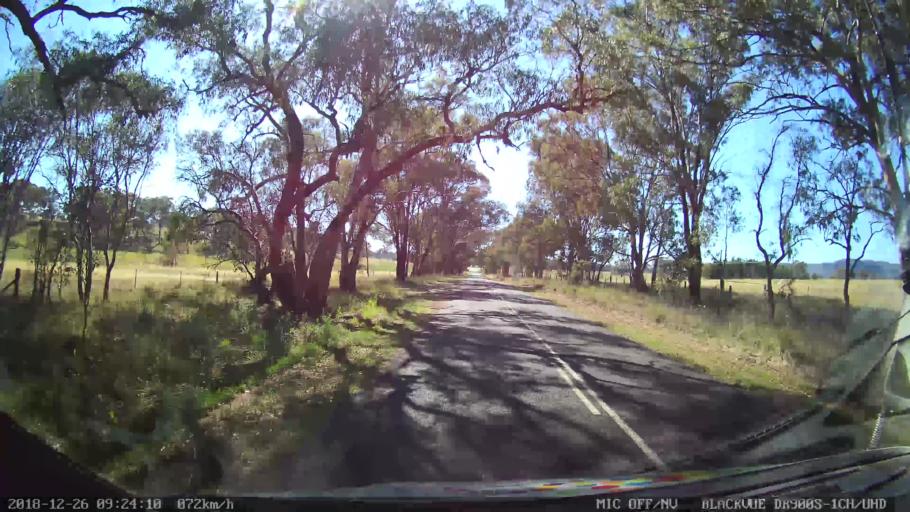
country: AU
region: New South Wales
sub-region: Mid-Western Regional
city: Kandos
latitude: -32.8096
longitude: 149.9953
